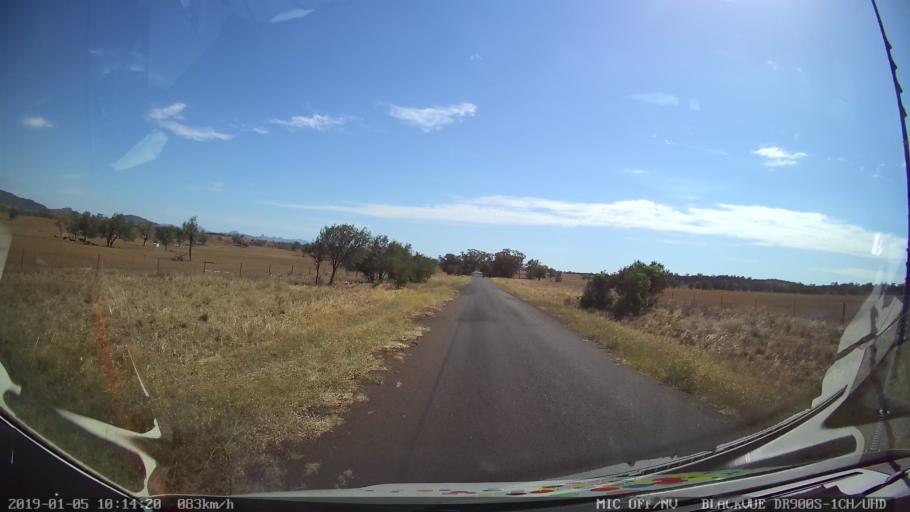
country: AU
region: New South Wales
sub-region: Gilgandra
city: Gilgandra
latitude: -31.5938
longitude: 148.9334
